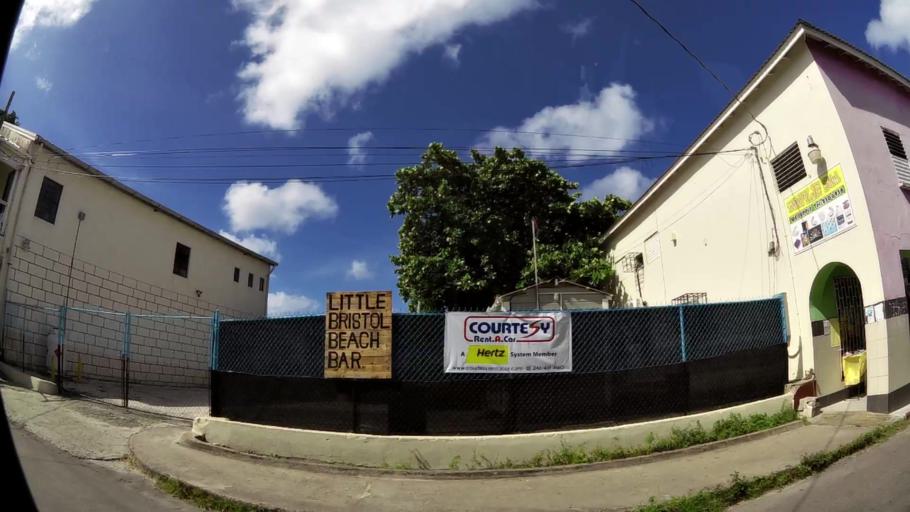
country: BB
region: Saint Peter
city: Speightstown
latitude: 13.2500
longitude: -59.6436
